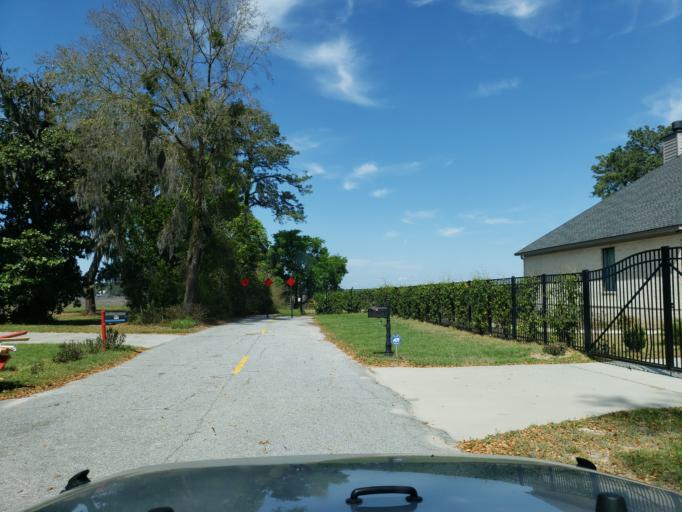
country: US
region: Georgia
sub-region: Chatham County
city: Montgomery
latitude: 31.9544
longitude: -81.1144
